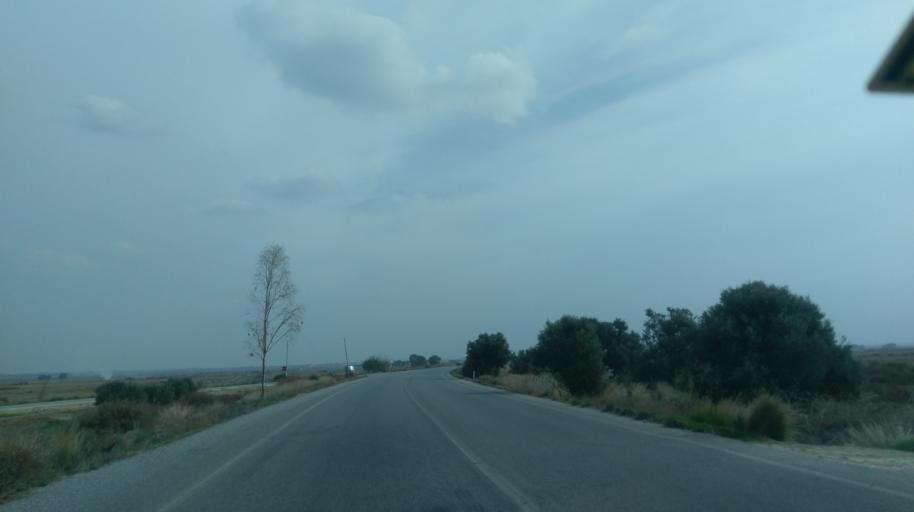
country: CY
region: Ammochostos
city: Lefkonoiko
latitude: 35.2602
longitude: 33.6676
